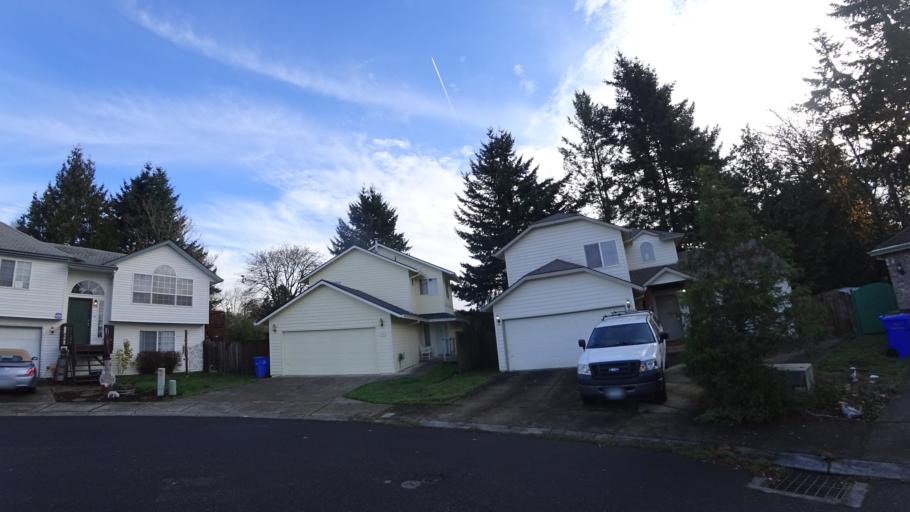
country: US
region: Oregon
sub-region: Multnomah County
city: Lents
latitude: 45.5243
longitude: -122.5270
